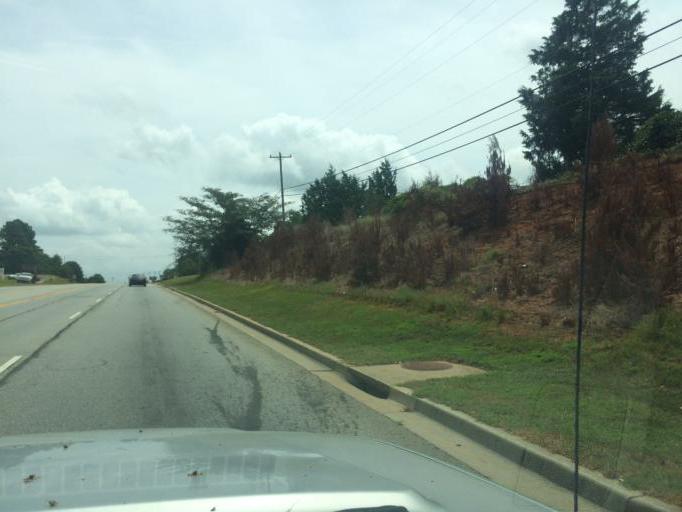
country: US
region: South Carolina
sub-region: Anderson County
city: Centerville
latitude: 34.5144
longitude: -82.7662
